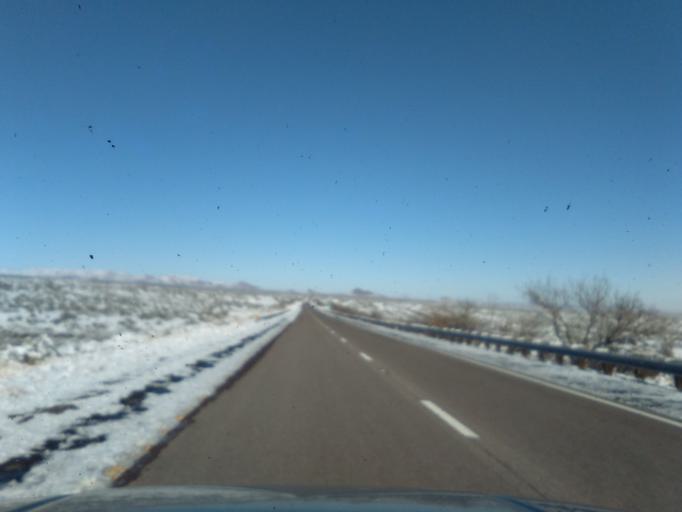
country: US
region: New Mexico
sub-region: Socorro County
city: Socorro
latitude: 33.6843
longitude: -107.0667
